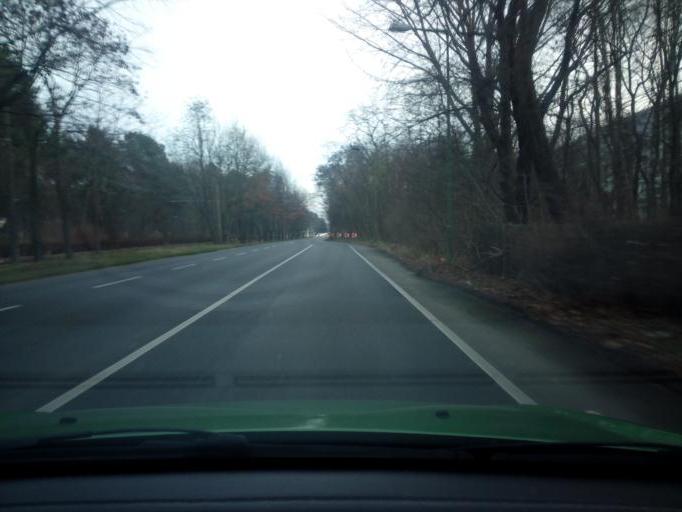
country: DE
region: Berlin
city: Berlin Koepenick
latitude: 52.4402
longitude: 13.5878
